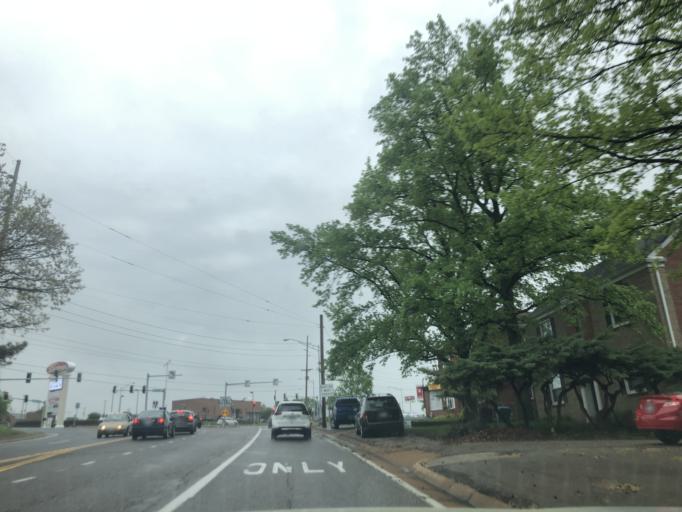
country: US
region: Missouri
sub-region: Saint Louis County
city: Shrewsbury
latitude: 38.5823
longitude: -90.3180
